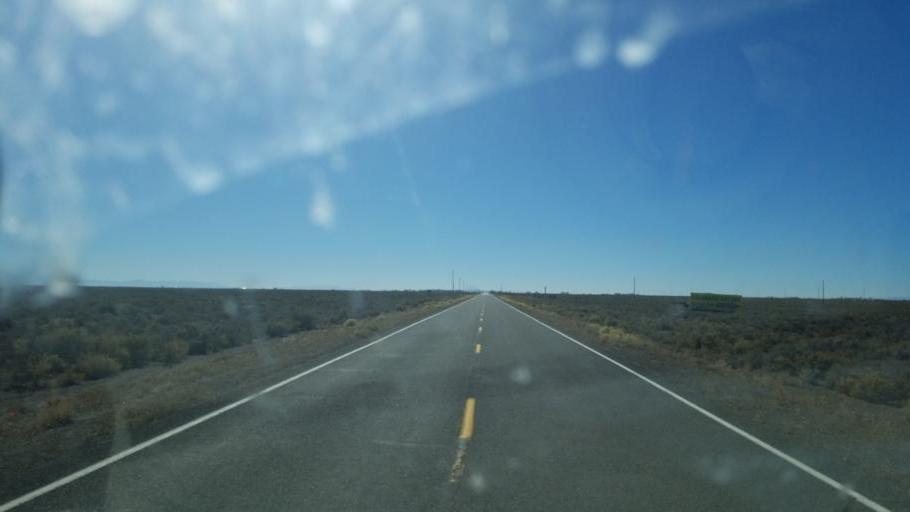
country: US
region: Colorado
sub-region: Saguache County
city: Center
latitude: 37.7890
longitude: -105.8852
